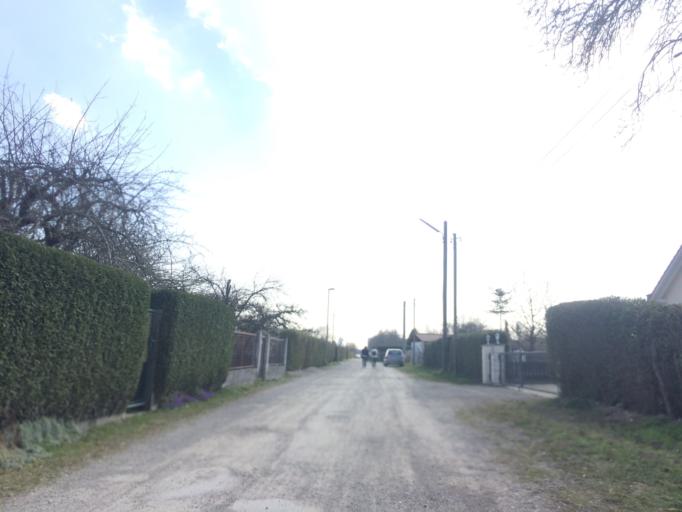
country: DE
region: Bavaria
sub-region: Swabia
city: Gersthofen
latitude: 48.3985
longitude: 10.8866
